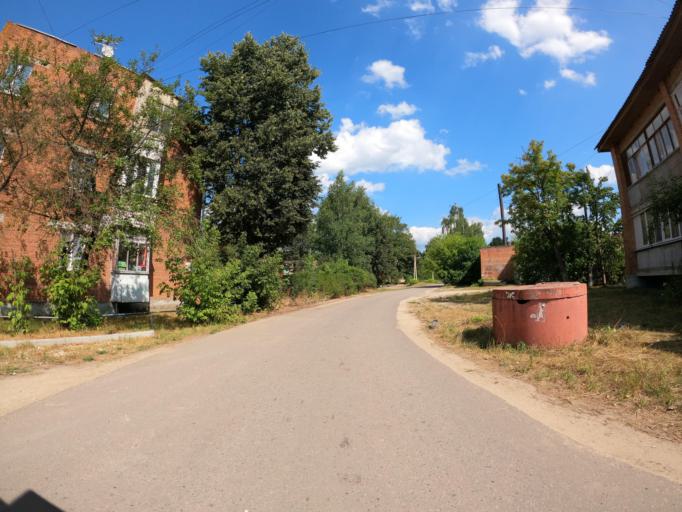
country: RU
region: Moskovskaya
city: Peski
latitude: 55.2627
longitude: 38.7641
